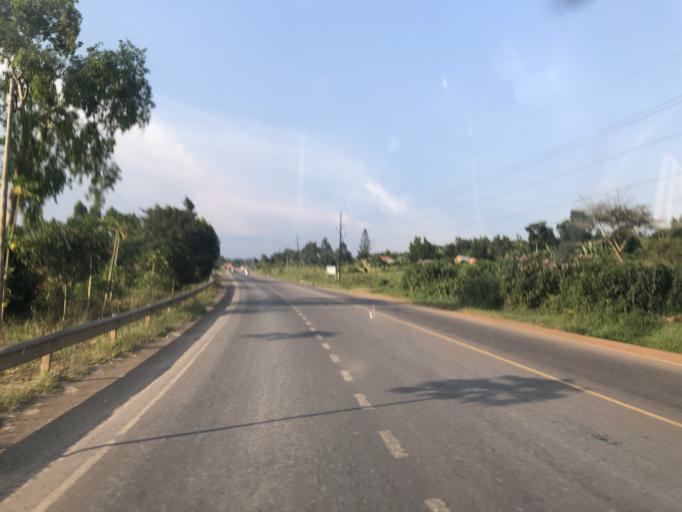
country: UG
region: Central Region
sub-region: Mpigi District
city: Mpigi
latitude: 0.1669
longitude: 32.2576
